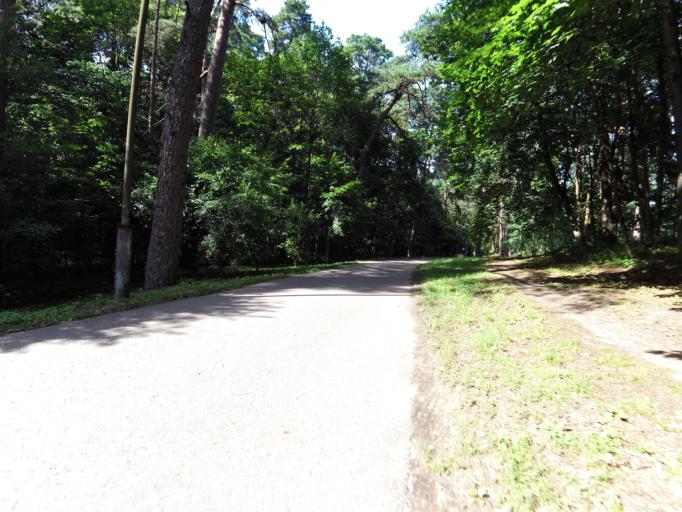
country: LT
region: Vilnius County
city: Vilkpede
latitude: 54.6876
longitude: 25.2433
